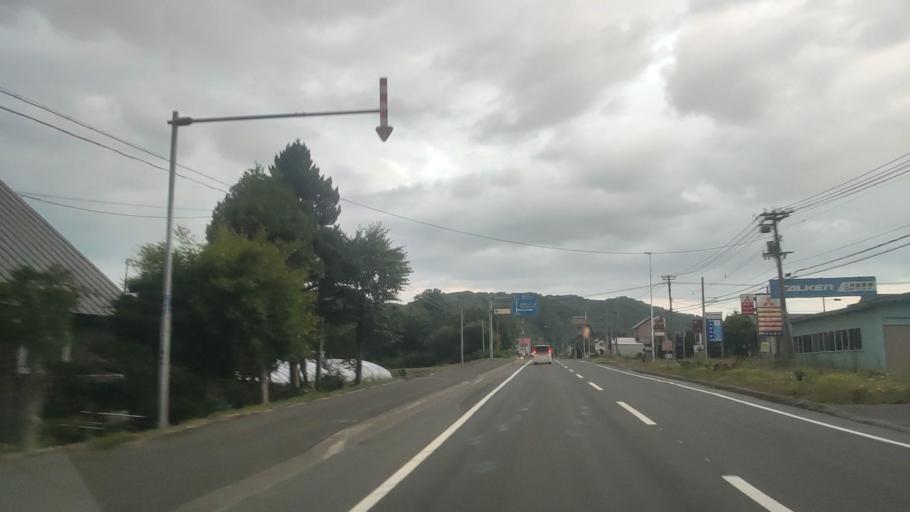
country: JP
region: Hokkaido
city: Shimo-furano
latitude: 43.3477
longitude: 142.3684
